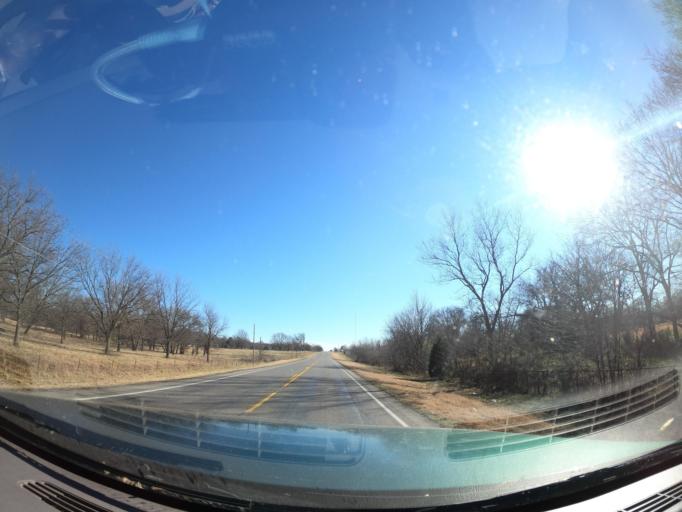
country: US
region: Oklahoma
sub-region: Muskogee County
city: Haskell
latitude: 35.7722
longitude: -95.6550
